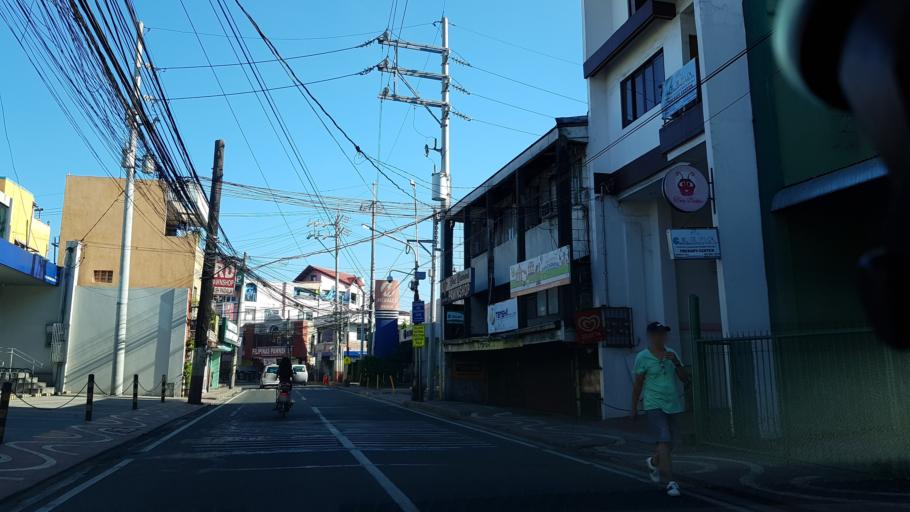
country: PH
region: Calabarzon
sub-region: Province of Rizal
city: Pateros
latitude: 14.5639
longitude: 121.0766
